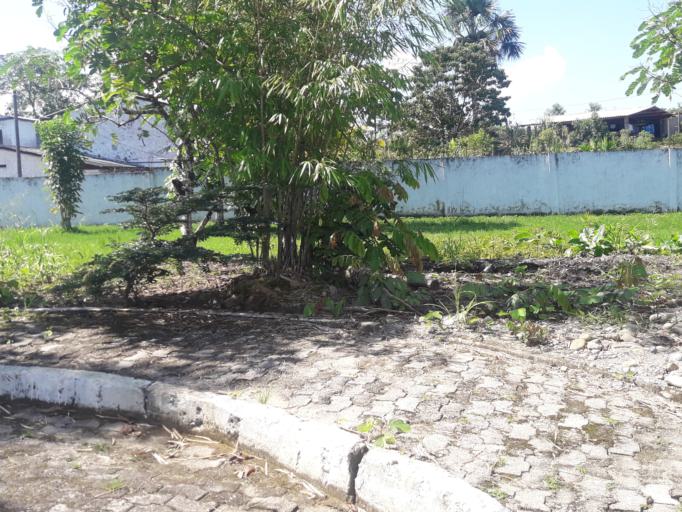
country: EC
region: Napo
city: Tena
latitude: -0.9746
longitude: -77.8161
